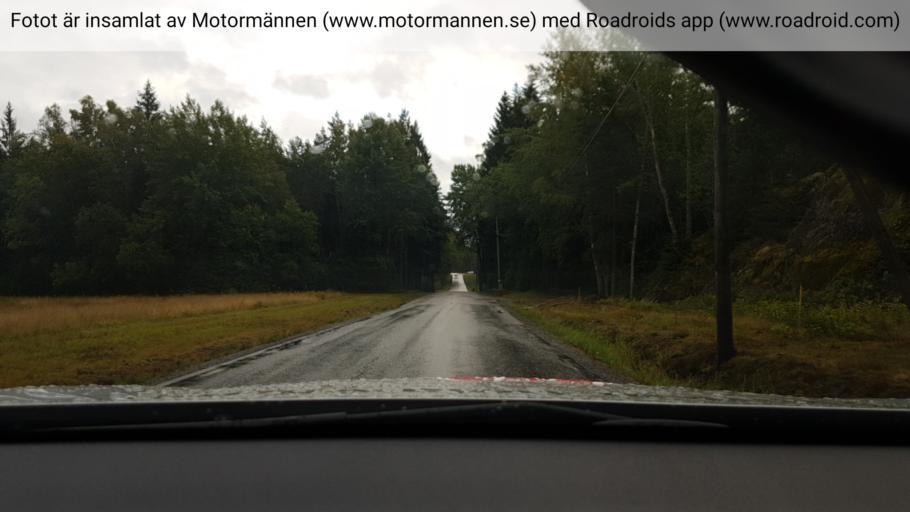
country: SE
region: Stockholm
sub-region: Haninge Kommun
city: Jordbro
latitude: 59.0894
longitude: 18.0439
